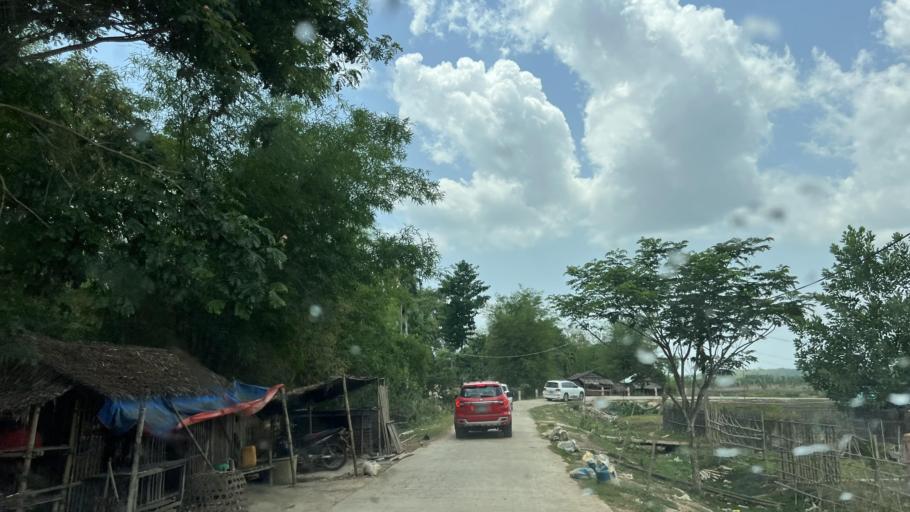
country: MM
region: Yangon
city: Twante
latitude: 16.5768
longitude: 95.9336
